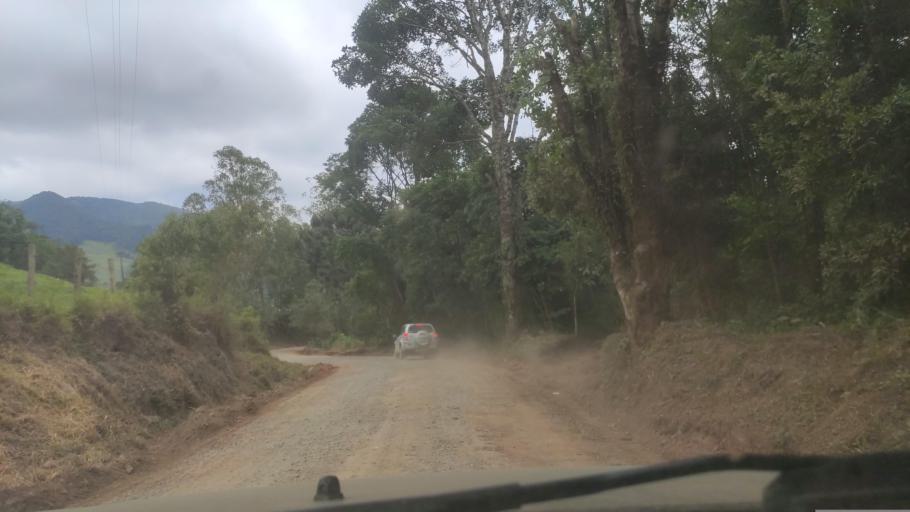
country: BR
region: Minas Gerais
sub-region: Cambui
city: Cambui
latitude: -22.6612
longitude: -45.9120
